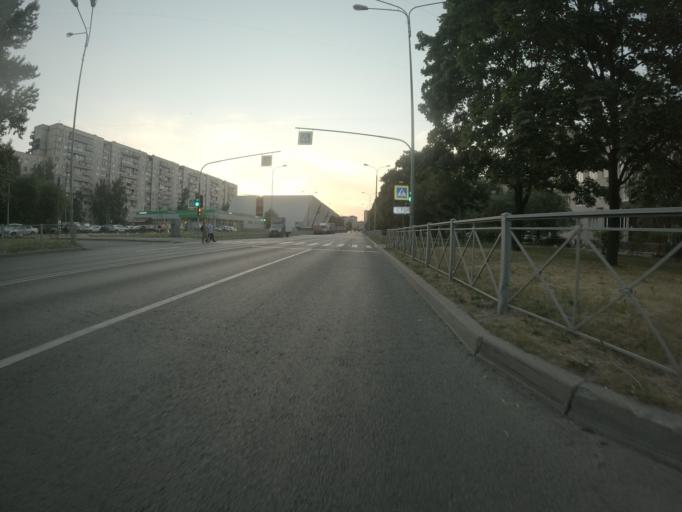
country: RU
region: St.-Petersburg
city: Krasnogvargeisky
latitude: 59.9117
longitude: 30.4613
